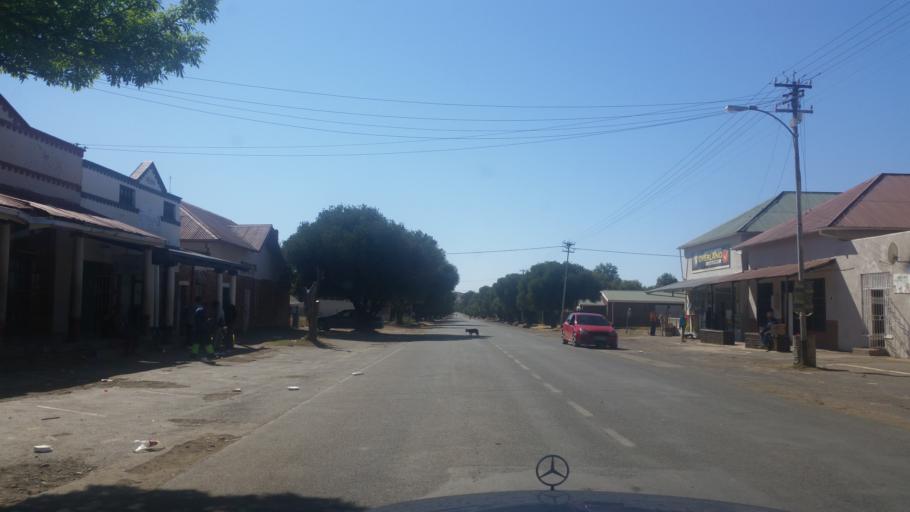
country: ZA
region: Orange Free State
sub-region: Xhariep District Municipality
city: Trompsburg
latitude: -30.4957
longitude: 25.9757
